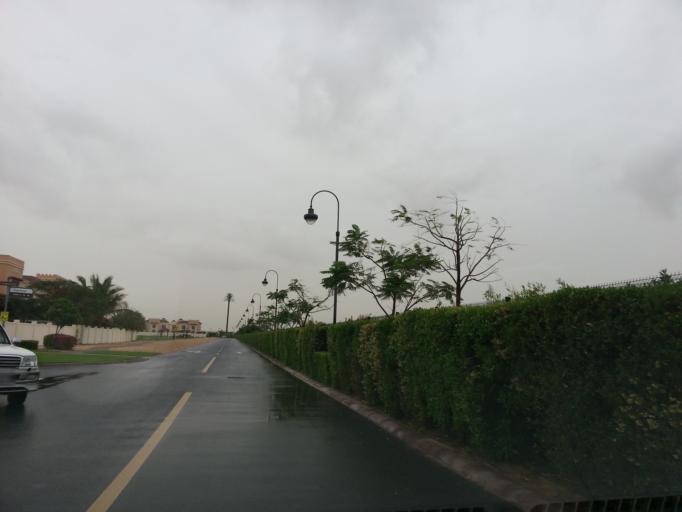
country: AE
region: Dubai
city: Dubai
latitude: 25.0306
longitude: 55.2084
